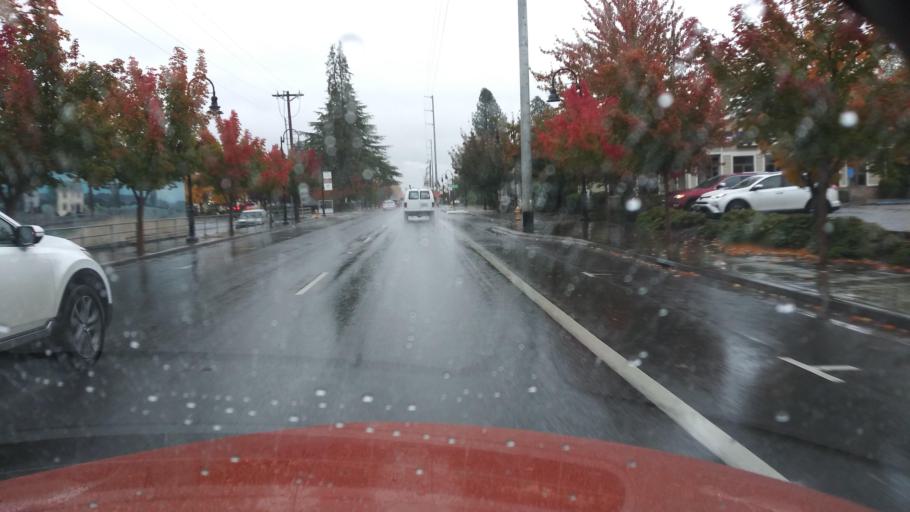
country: US
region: Oregon
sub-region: Washington County
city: Cornelius
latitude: 45.5201
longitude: -123.0525
